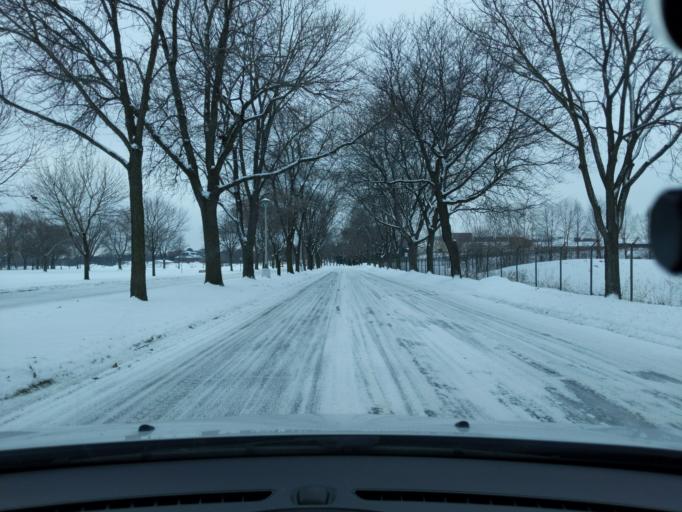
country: US
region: Minnesota
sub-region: Ramsey County
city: Falcon Heights
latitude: 44.9844
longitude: -93.1723
